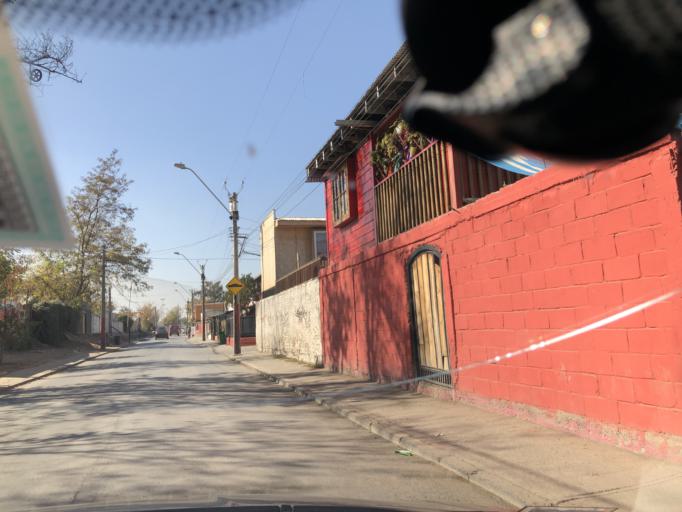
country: CL
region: Santiago Metropolitan
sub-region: Provincia de Santiago
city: La Pintana
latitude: -33.5864
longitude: -70.6053
